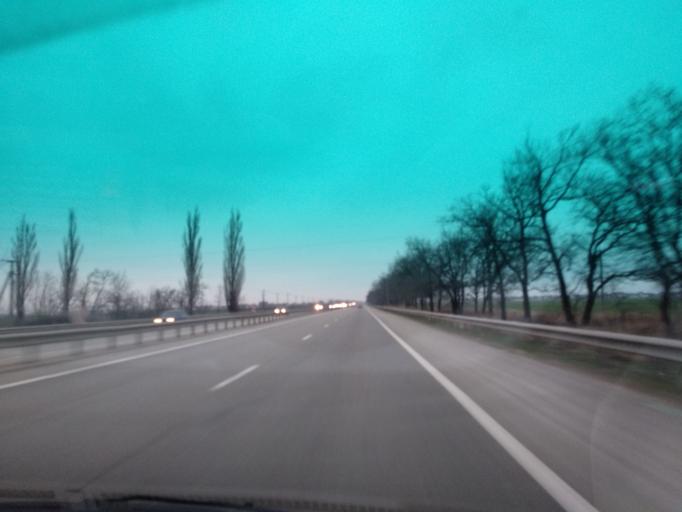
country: RU
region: Krasnodarskiy
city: Pashkovskiy
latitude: 45.0749
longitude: 39.1360
